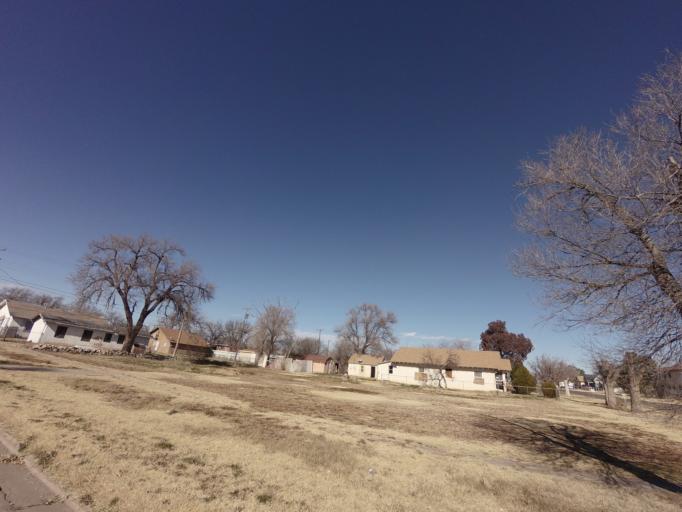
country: US
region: New Mexico
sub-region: Curry County
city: Clovis
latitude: 34.4018
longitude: -103.2106
